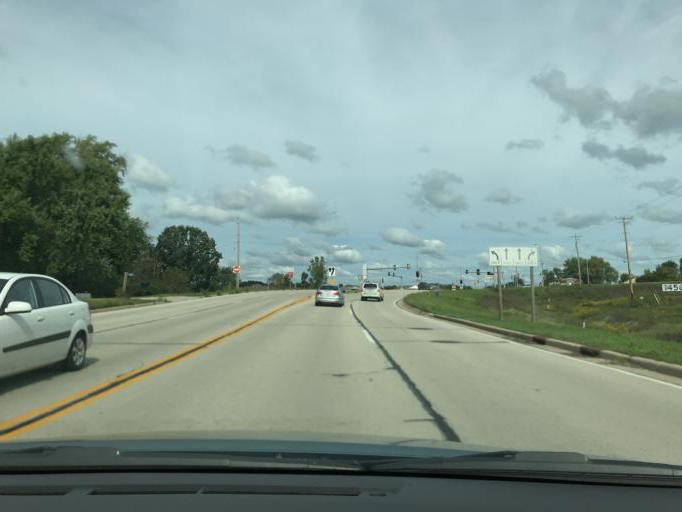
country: US
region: Wisconsin
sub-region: Racine County
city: Burlington
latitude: 42.6560
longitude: -88.2593
